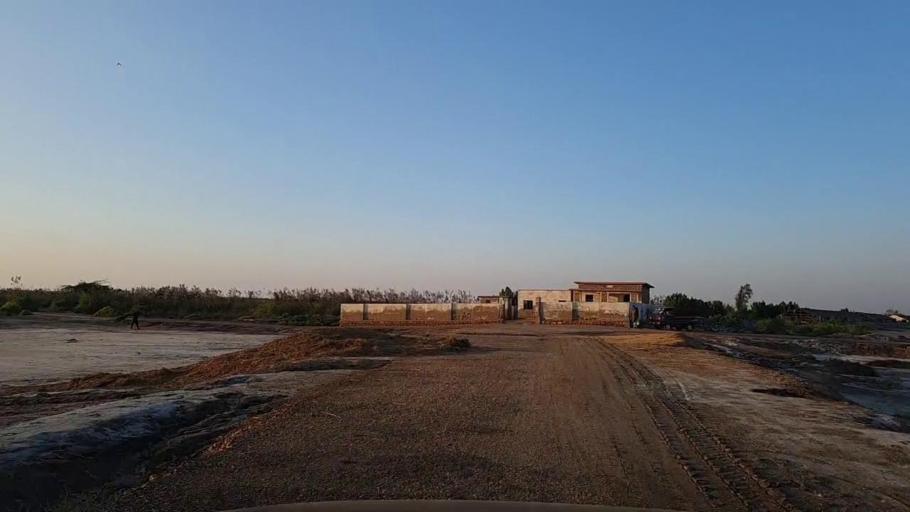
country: PK
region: Sindh
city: Thatta
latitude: 24.6633
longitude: 67.9171
